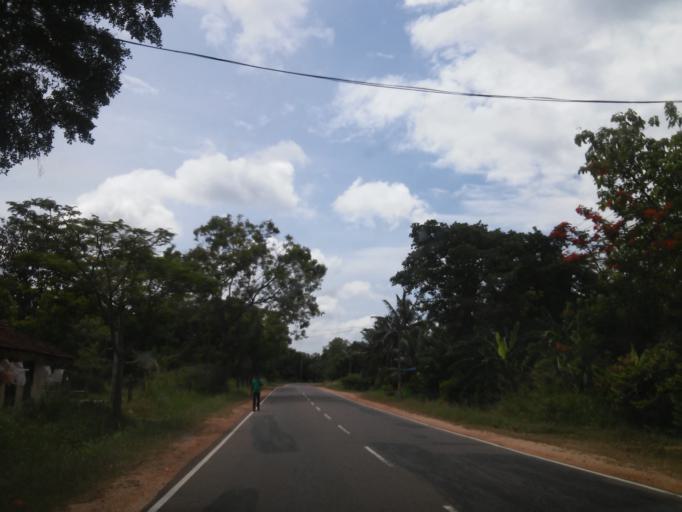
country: LK
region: Central
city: Sigiriya
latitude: 8.0590
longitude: 80.7157
